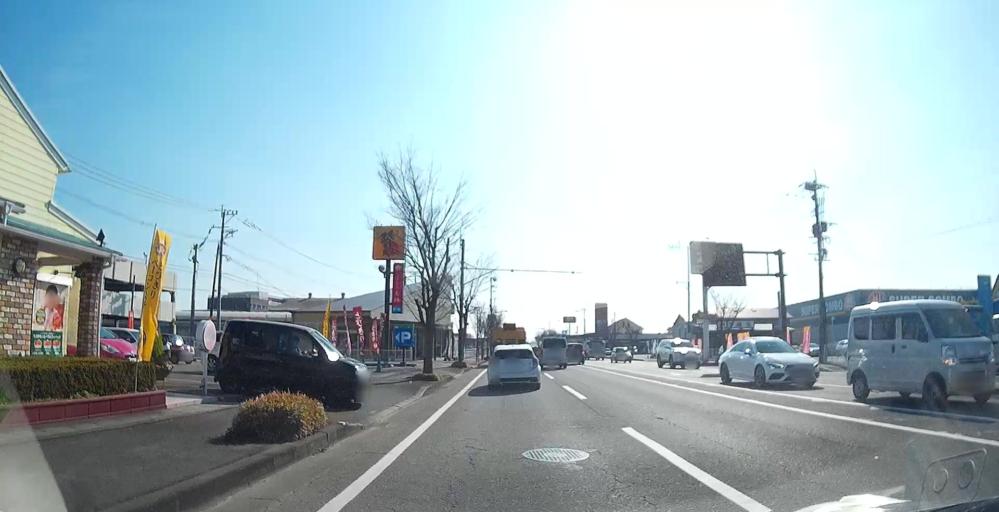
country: JP
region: Kumamoto
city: Kumamoto
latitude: 32.7830
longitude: 130.6734
